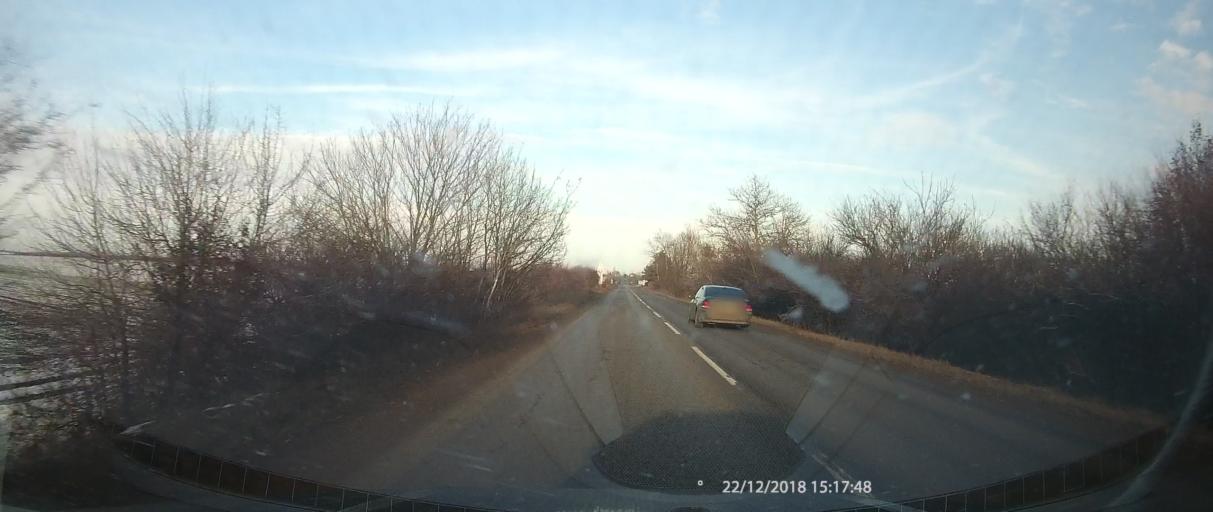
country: BG
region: Ruse
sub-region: Obshtina Dve Mogili
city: Dve Mogili
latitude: 43.6303
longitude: 25.8644
